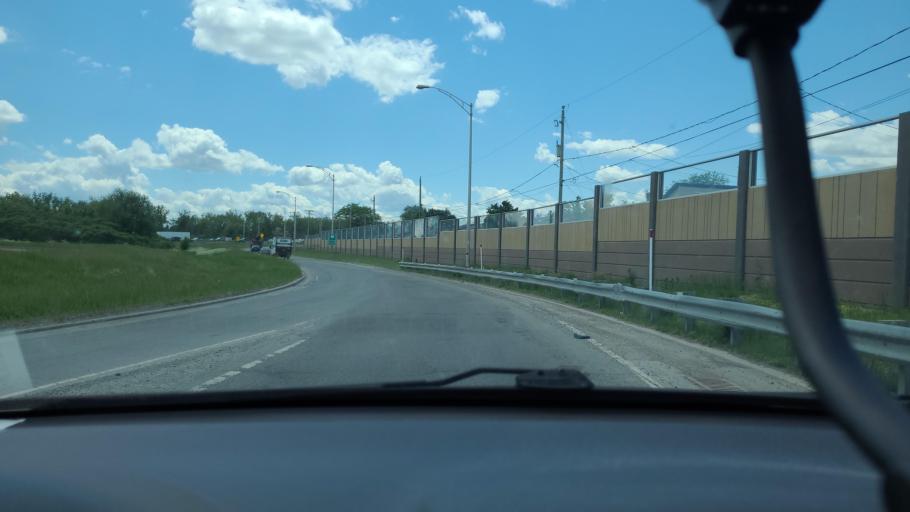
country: CA
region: Quebec
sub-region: Laval
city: Laval
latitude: 45.5937
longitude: -73.7195
